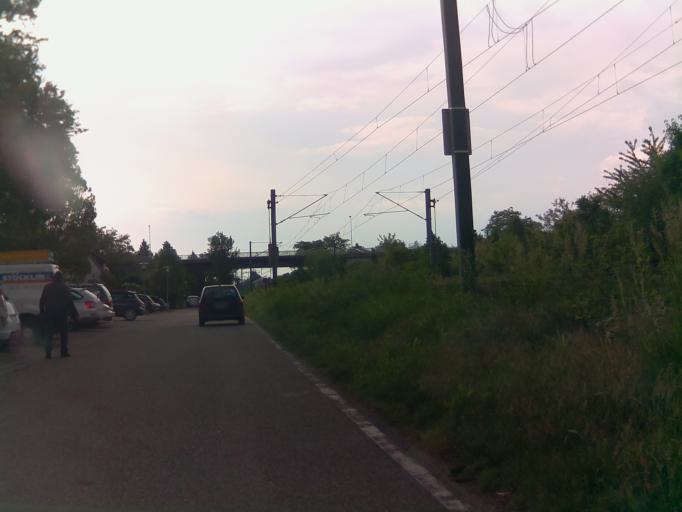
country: DE
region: Rheinland-Pfalz
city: Schifferstadt
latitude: 49.3701
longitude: 8.3812
